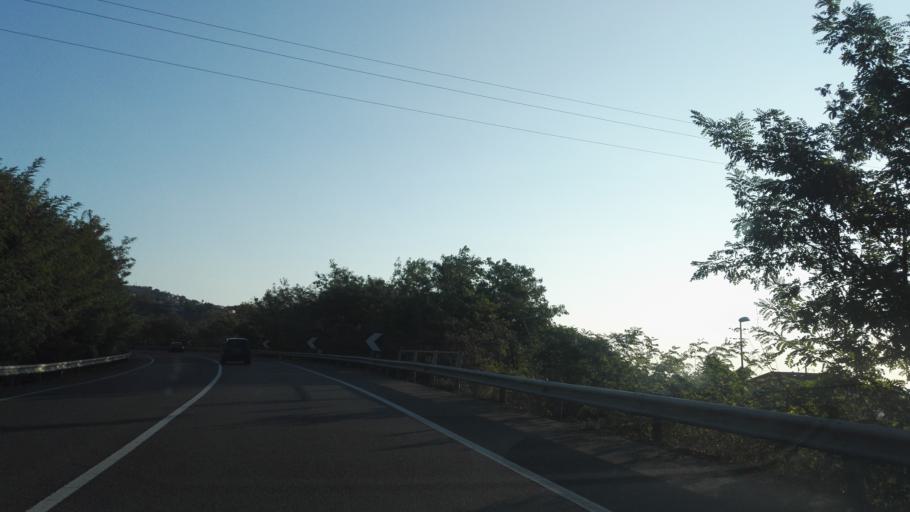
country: IT
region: Calabria
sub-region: Provincia di Catanzaro
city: Montepaone Lido
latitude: 38.7367
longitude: 16.5455
